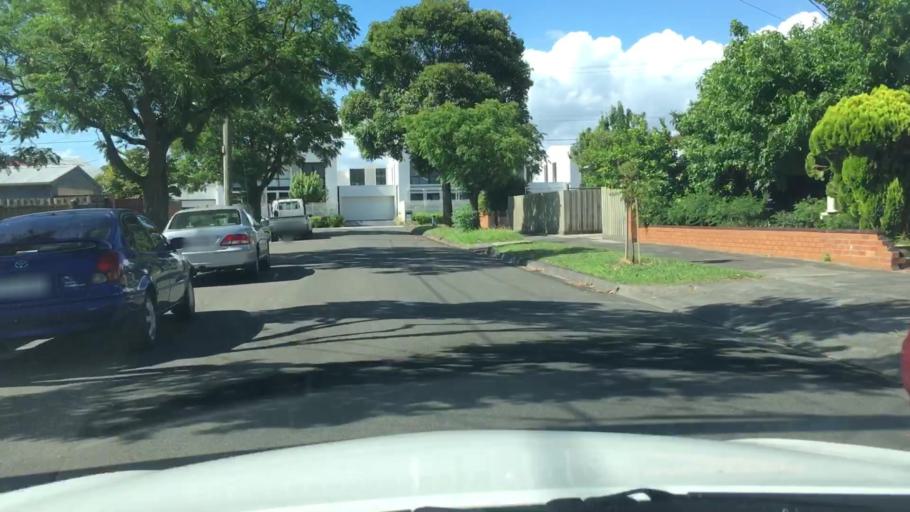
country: AU
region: Victoria
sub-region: Greater Dandenong
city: Springvale
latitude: -37.9487
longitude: 145.1429
